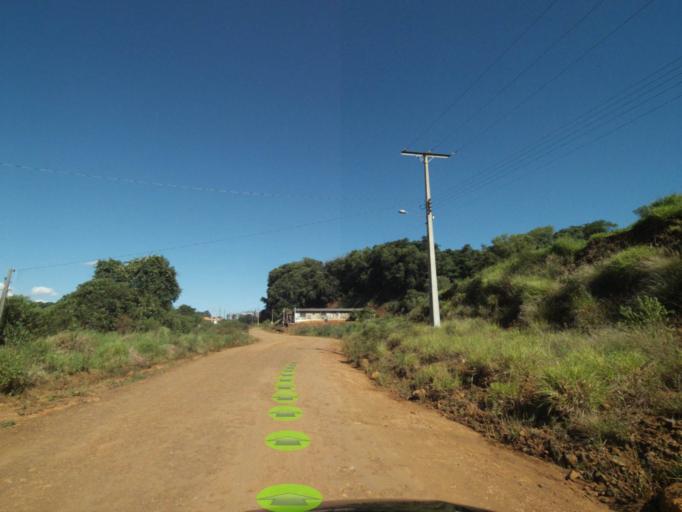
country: BR
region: Parana
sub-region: Coronel Vivida
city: Coronel Vivida
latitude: -26.1436
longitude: -52.3772
